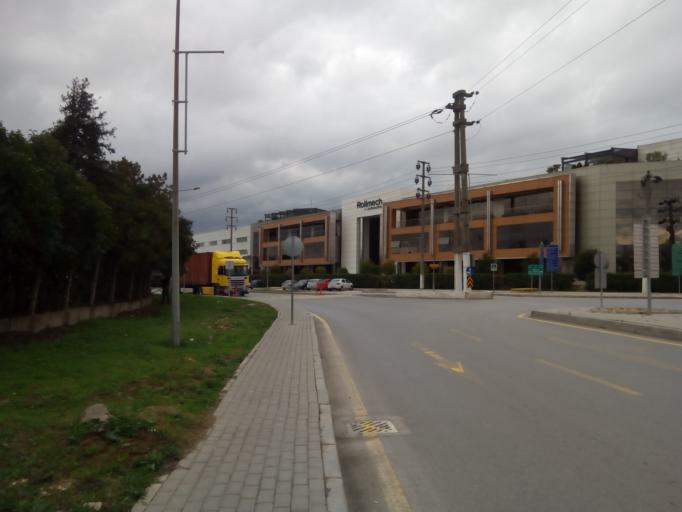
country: TR
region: Bursa
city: Niluefer
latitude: 40.2478
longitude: 28.9559
